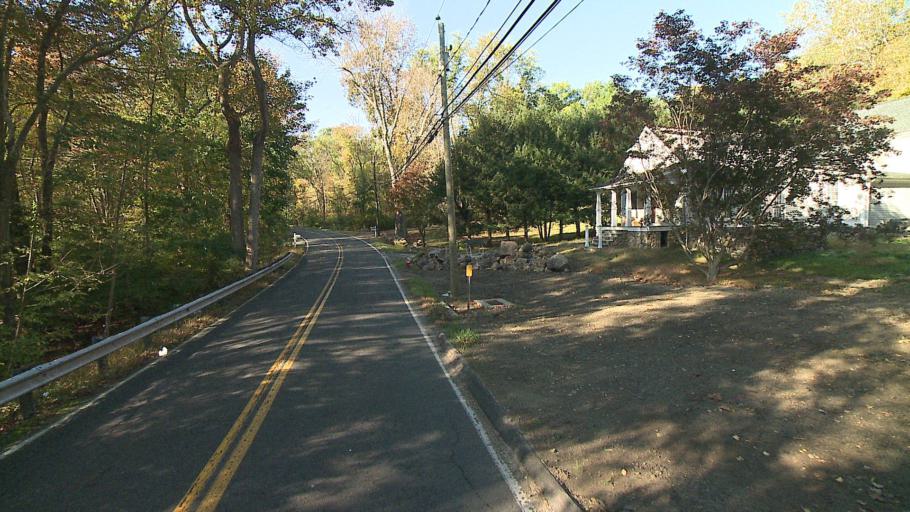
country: US
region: Connecticut
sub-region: Fairfield County
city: Wilton
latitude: 41.1973
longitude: -73.3952
